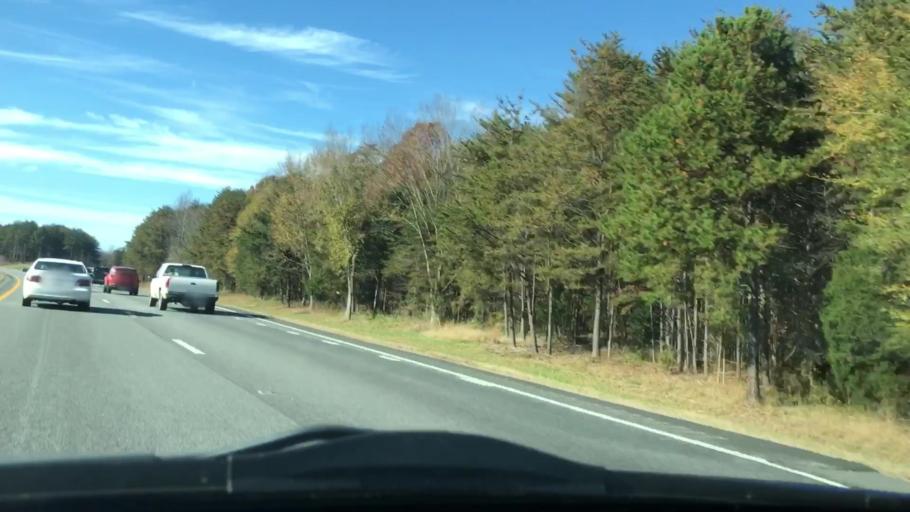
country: US
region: North Carolina
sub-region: Guilford County
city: High Point
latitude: 36.0241
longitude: -80.0535
